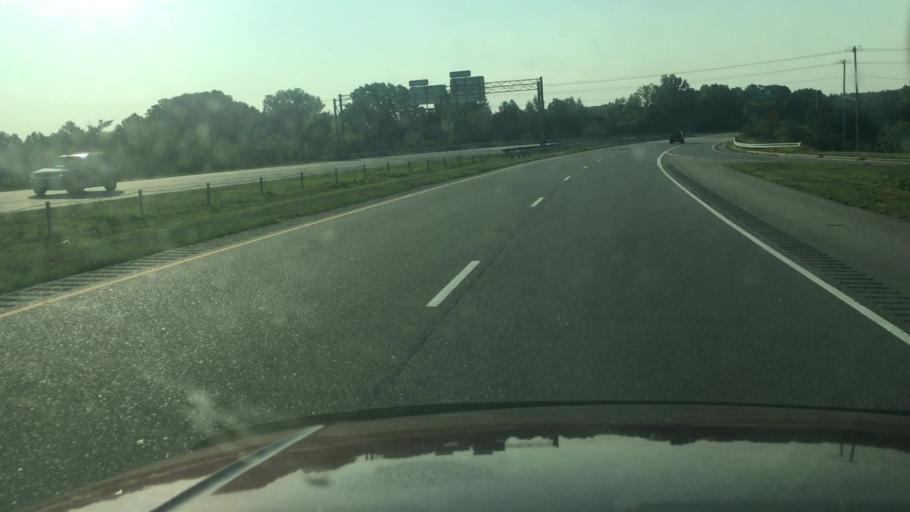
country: US
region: North Carolina
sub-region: Cumberland County
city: Fayetteville
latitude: 35.0379
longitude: -78.8852
